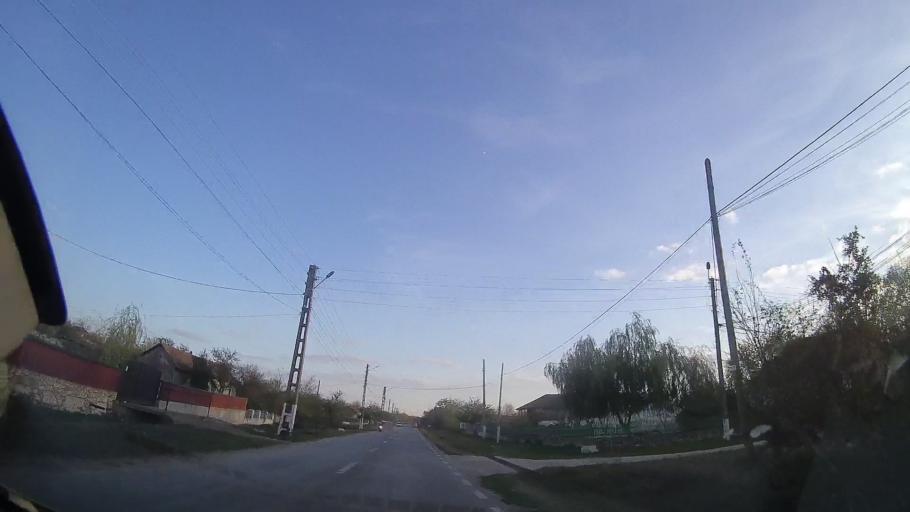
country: RO
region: Constanta
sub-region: Comuna Chirnogeni
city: Plopeni
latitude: 43.9495
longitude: 28.1986
